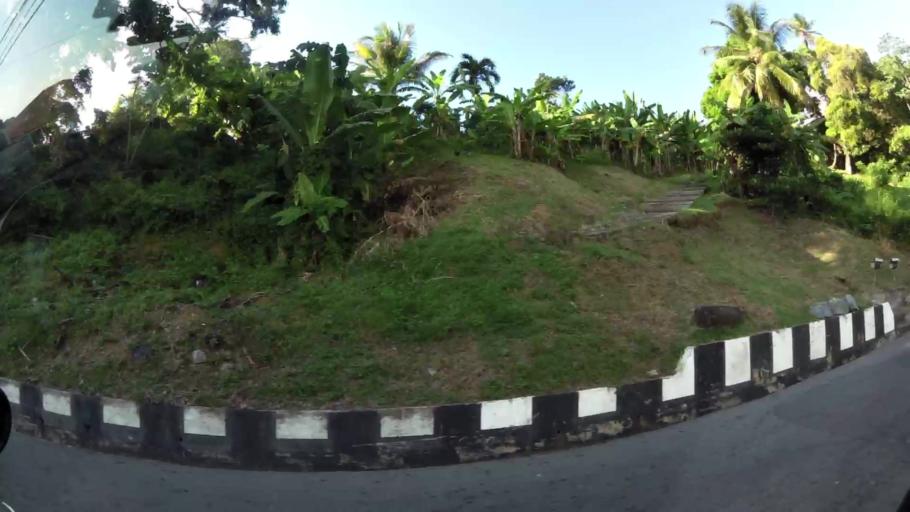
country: TT
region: Tobago
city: Scarborough
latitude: 11.1926
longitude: -60.6825
